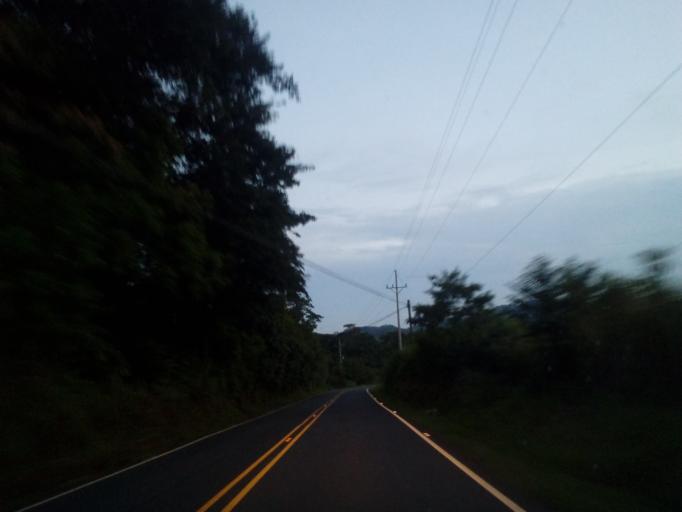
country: CR
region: Guanacaste
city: Samara
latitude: 9.9606
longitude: -85.5160
